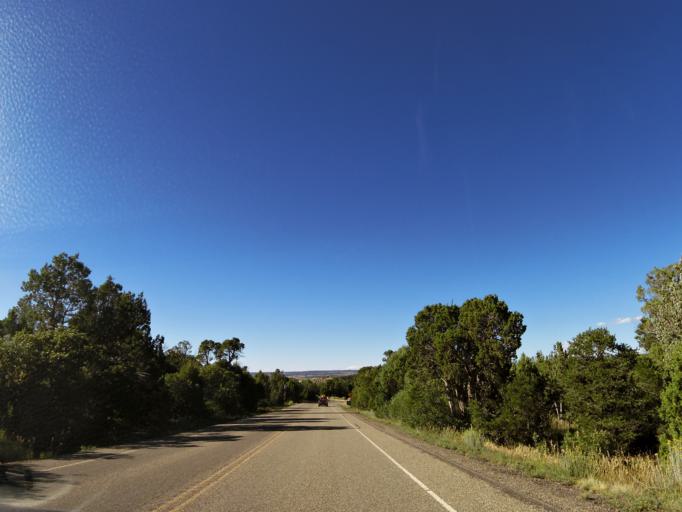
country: US
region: Colorado
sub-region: Montezuma County
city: Mancos
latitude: 37.3372
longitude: -108.4116
